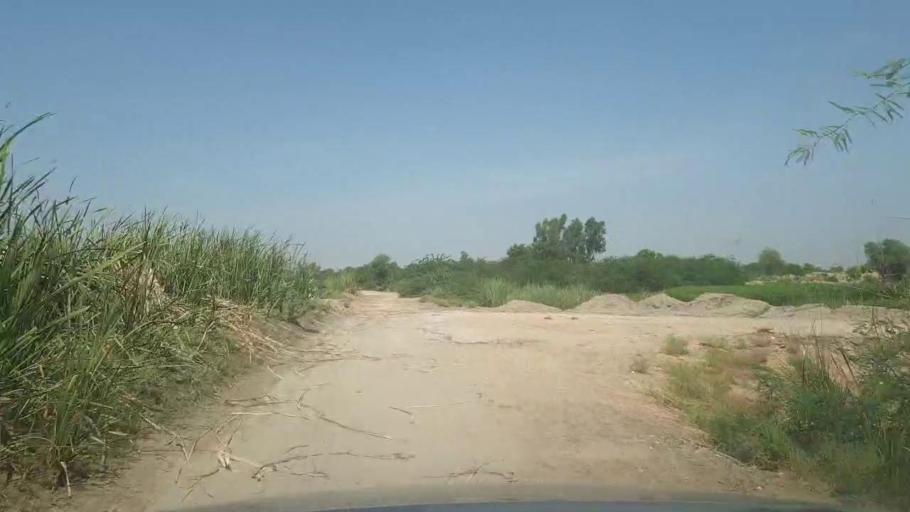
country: PK
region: Sindh
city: Khairpur
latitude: 27.4000
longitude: 69.0437
